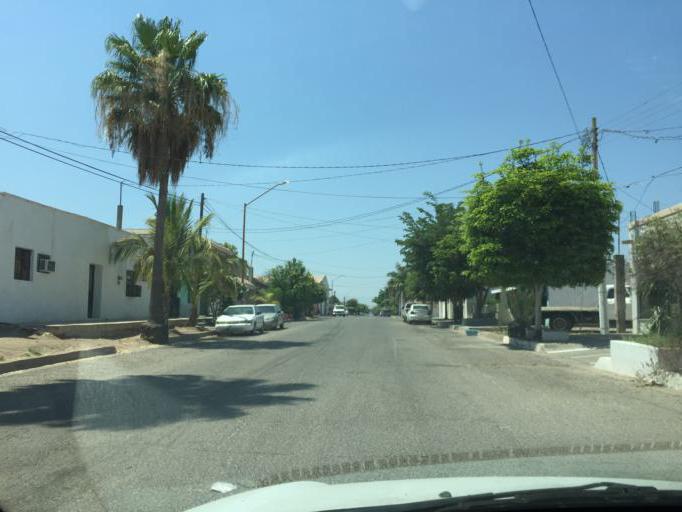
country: MX
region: Sonora
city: Navojoa
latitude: 27.0799
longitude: -109.4571
